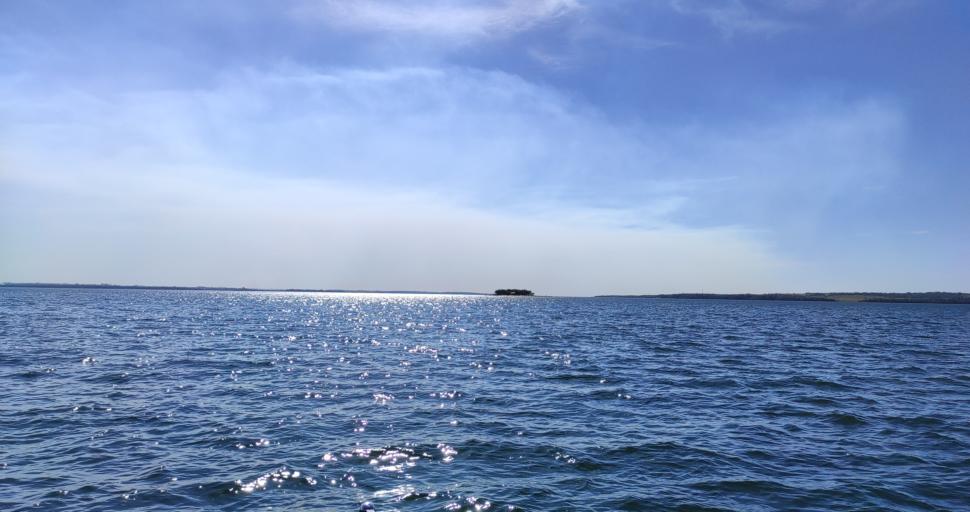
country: AR
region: Misiones
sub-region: Departamento de Capital
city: Posadas
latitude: -27.3434
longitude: -55.9363
